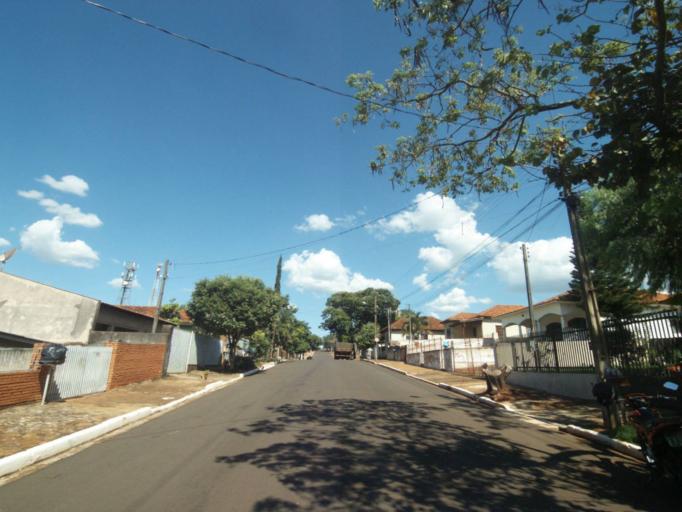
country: BR
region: Parana
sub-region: Sertanopolis
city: Sertanopolis
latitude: -23.0409
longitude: -50.8187
